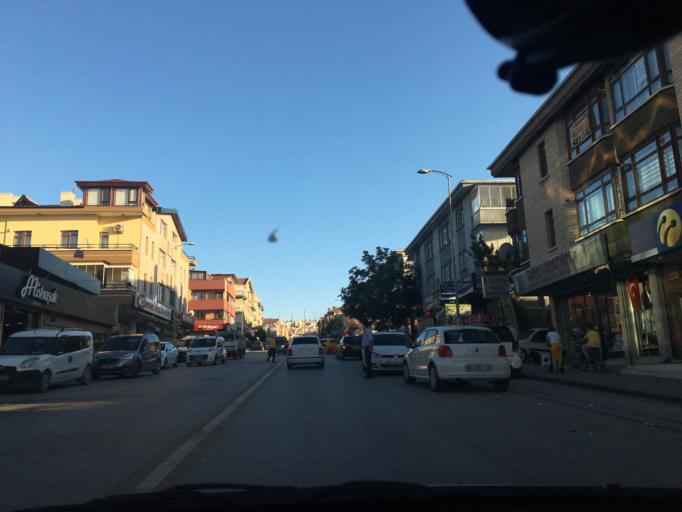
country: TR
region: Ankara
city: Ankara
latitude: 39.8910
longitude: 32.8290
